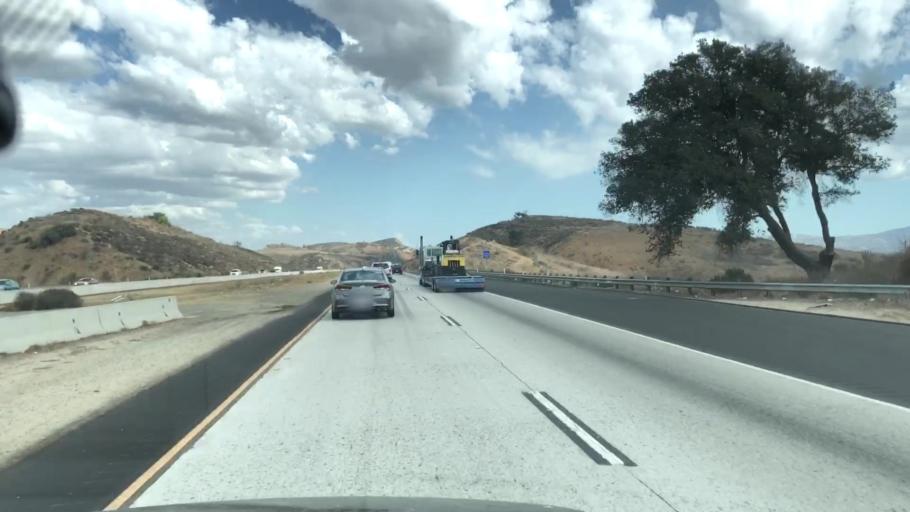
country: US
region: California
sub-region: Ventura County
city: Simi Valley
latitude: 34.2906
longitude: -118.8202
